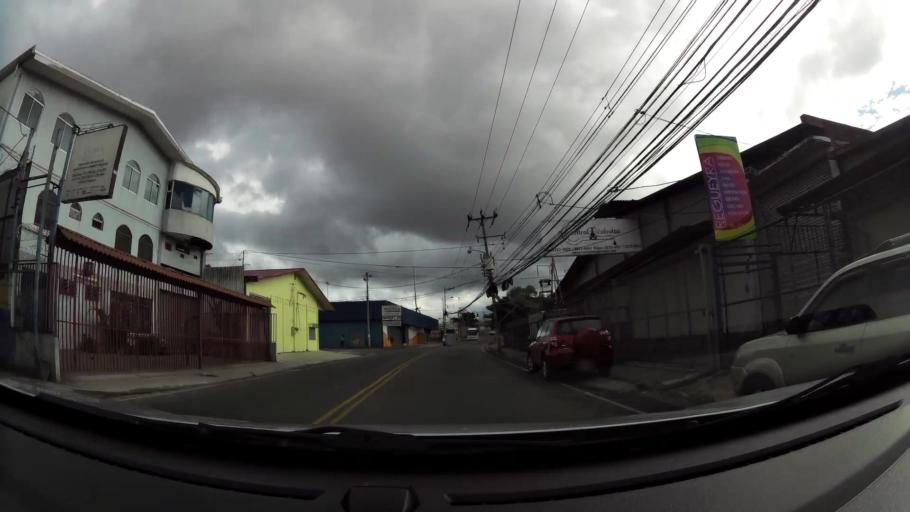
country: CR
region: San Jose
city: Curridabat
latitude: 9.9107
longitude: -84.0459
